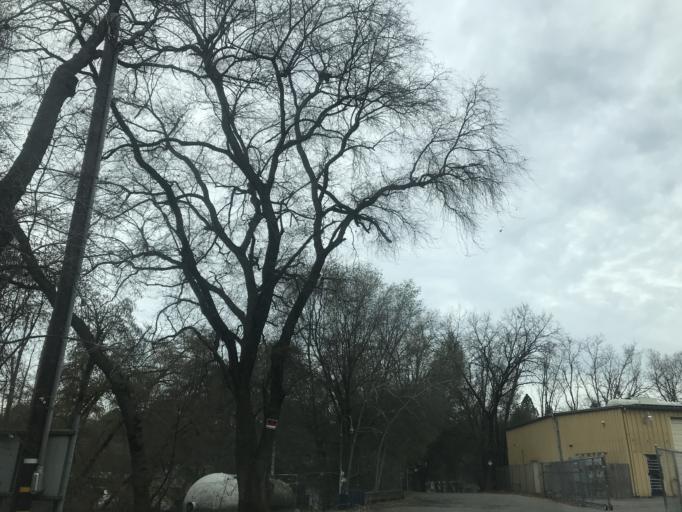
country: US
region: California
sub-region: El Dorado County
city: Placerville
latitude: 38.7342
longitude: -120.8303
